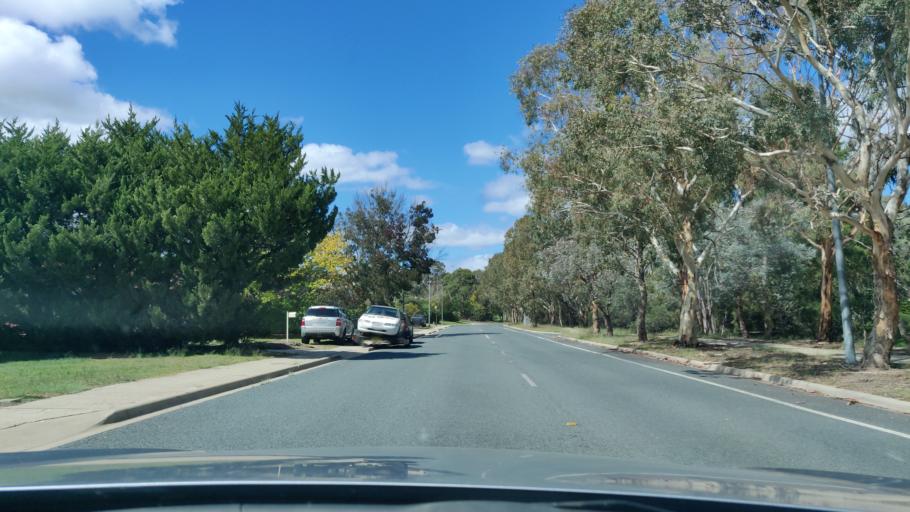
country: AU
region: Australian Capital Territory
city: Macarthur
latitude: -35.4411
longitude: 149.1000
